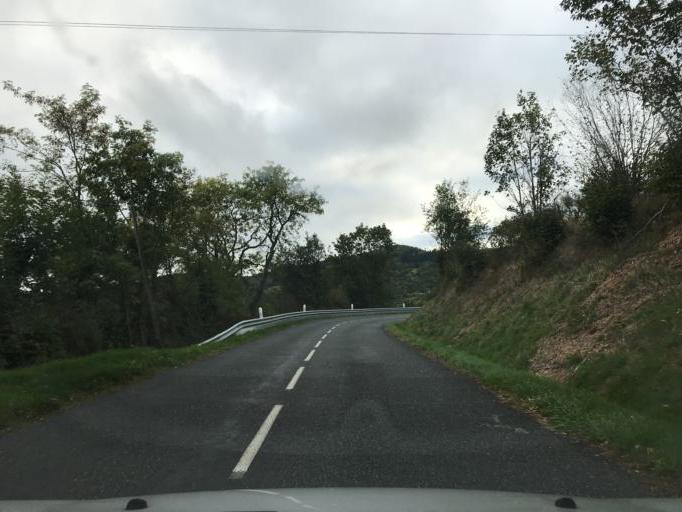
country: FR
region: Rhone-Alpes
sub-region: Departement du Rhone
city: Le Perreon
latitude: 46.0234
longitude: 4.5666
